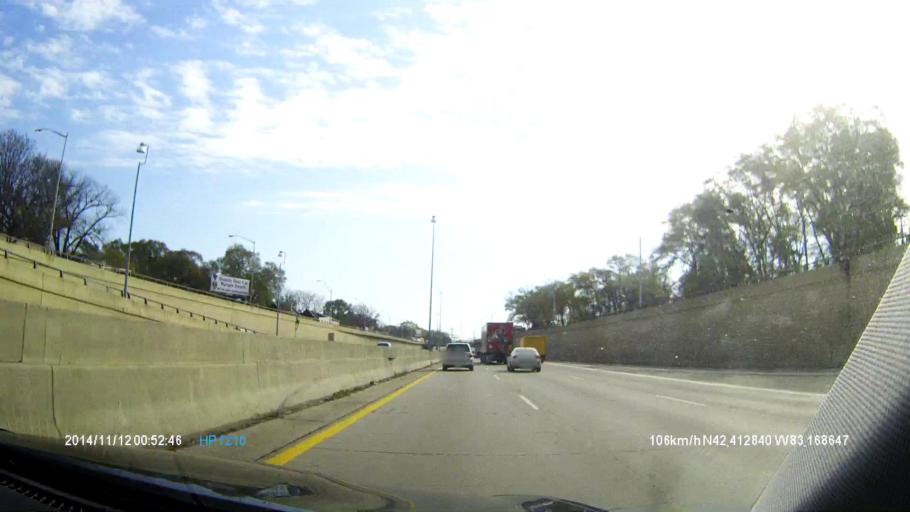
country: US
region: Michigan
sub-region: Oakland County
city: Oak Park
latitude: 42.4127
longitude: -83.1684
